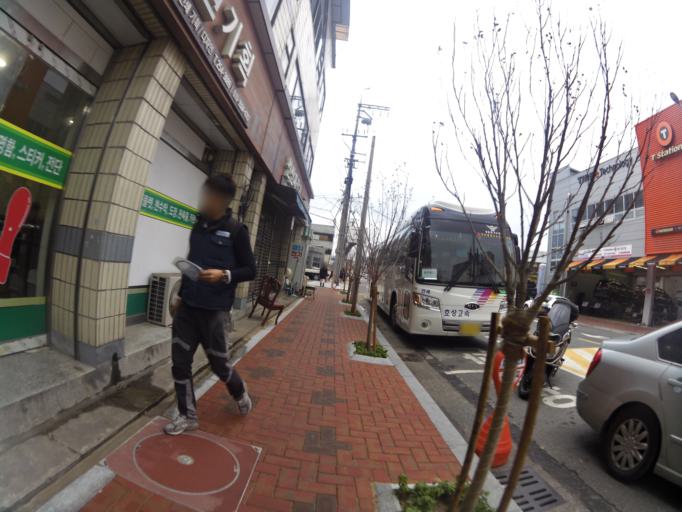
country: KR
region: Daegu
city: Daegu
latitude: 35.8678
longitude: 128.5866
